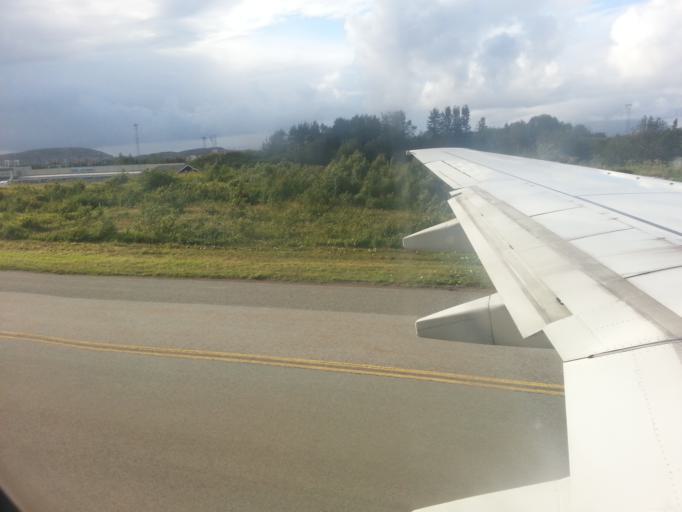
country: NO
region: Nordland
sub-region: Bodo
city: Bodo
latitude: 67.2714
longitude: 14.3756
